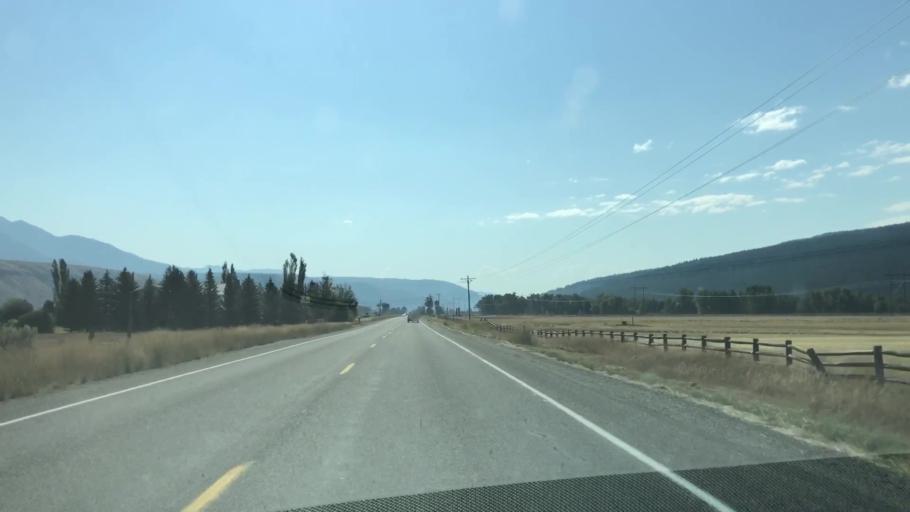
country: US
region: Idaho
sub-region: Teton County
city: Victor
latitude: 43.3989
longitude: -111.2839
